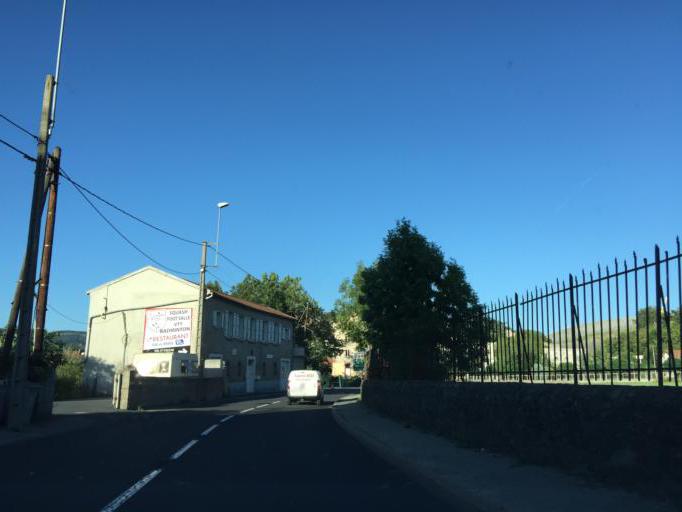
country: FR
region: Auvergne
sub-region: Departement de la Haute-Loire
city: Chadrac
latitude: 45.0501
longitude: 3.8974
